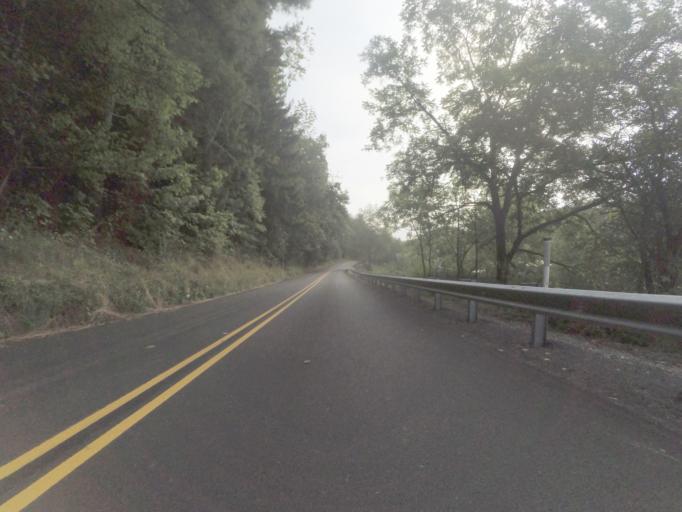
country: US
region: Pennsylvania
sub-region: Centre County
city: Milesburg
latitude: 41.0019
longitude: -77.8000
